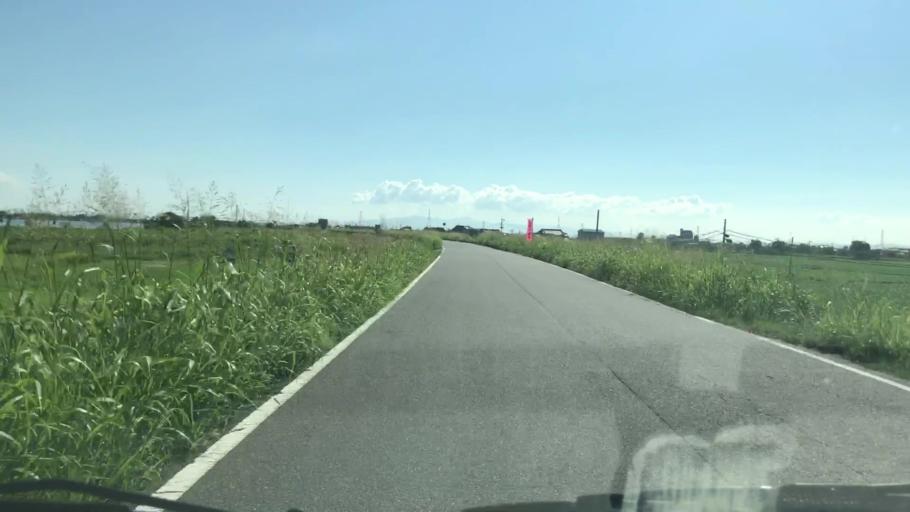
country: JP
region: Saga Prefecture
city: Kanzakimachi-kanzaki
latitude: 33.2691
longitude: 130.4232
